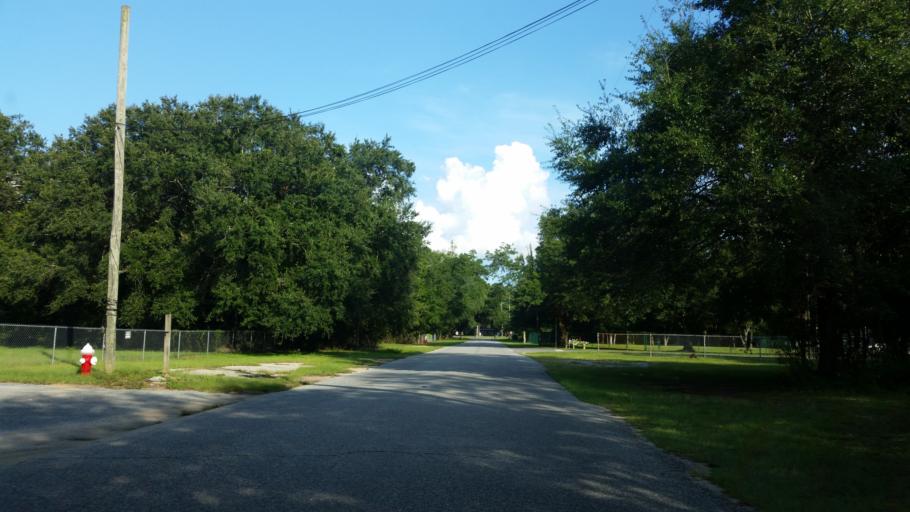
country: US
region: Florida
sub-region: Escambia County
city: Ferry Pass
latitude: 30.4840
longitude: -87.1995
